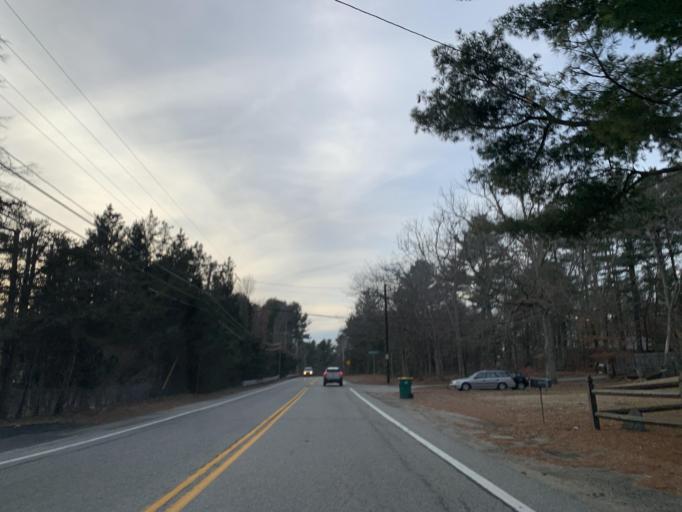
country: US
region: Rhode Island
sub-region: Providence County
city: Chepachet
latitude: 41.9054
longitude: -71.6536
